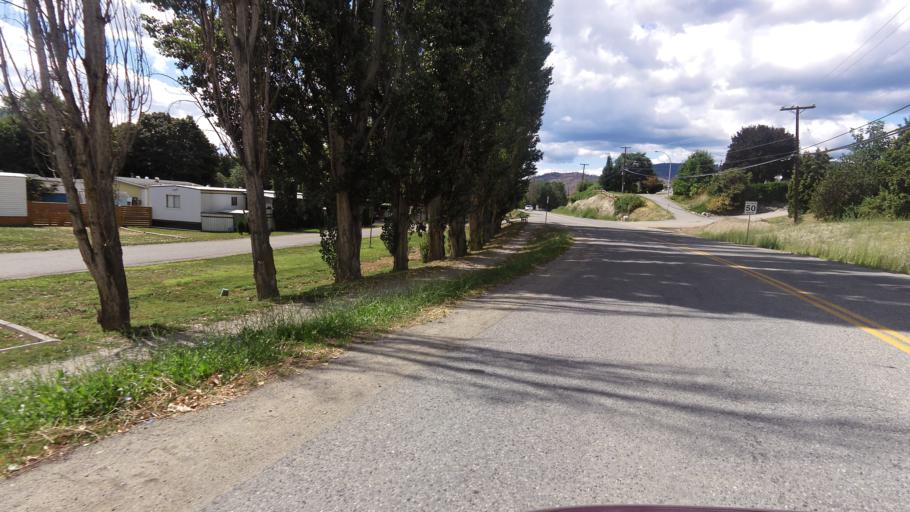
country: CA
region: British Columbia
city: West Kelowna
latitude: 49.8265
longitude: -119.6044
